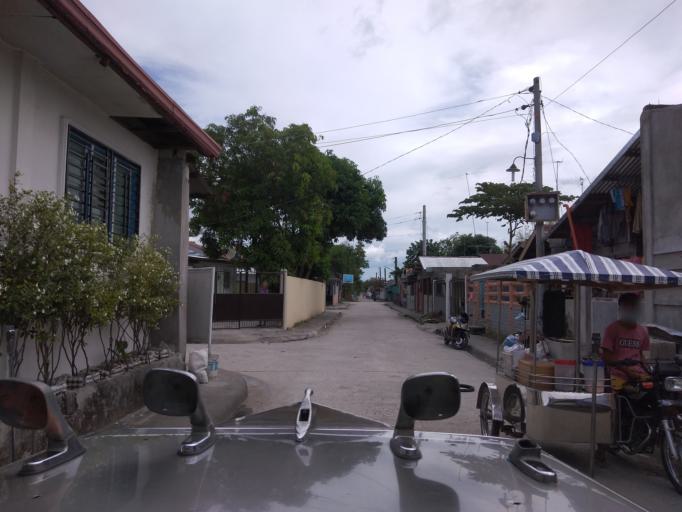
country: PH
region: Central Luzon
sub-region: Province of Pampanga
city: Pandacaqui
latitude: 15.1766
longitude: 120.6582
